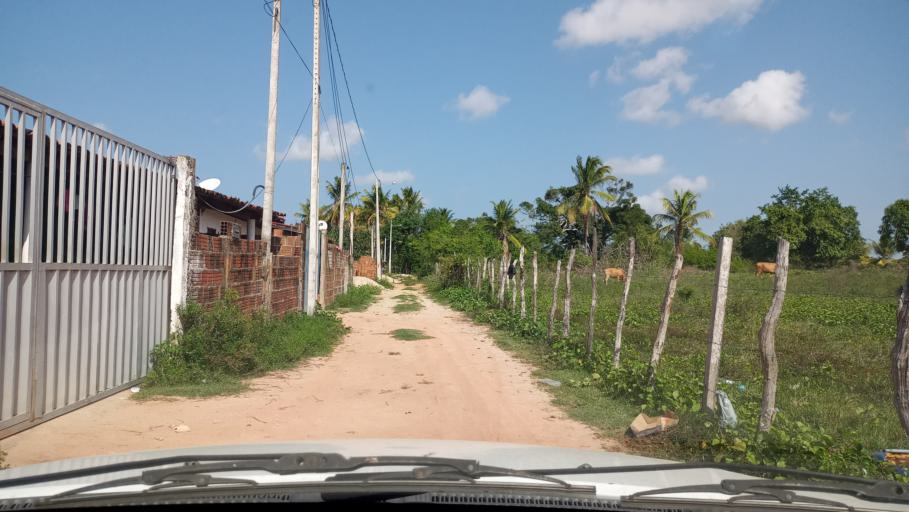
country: BR
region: Rio Grande do Norte
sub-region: Ares
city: Ares
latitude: -6.2239
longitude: -35.1514
